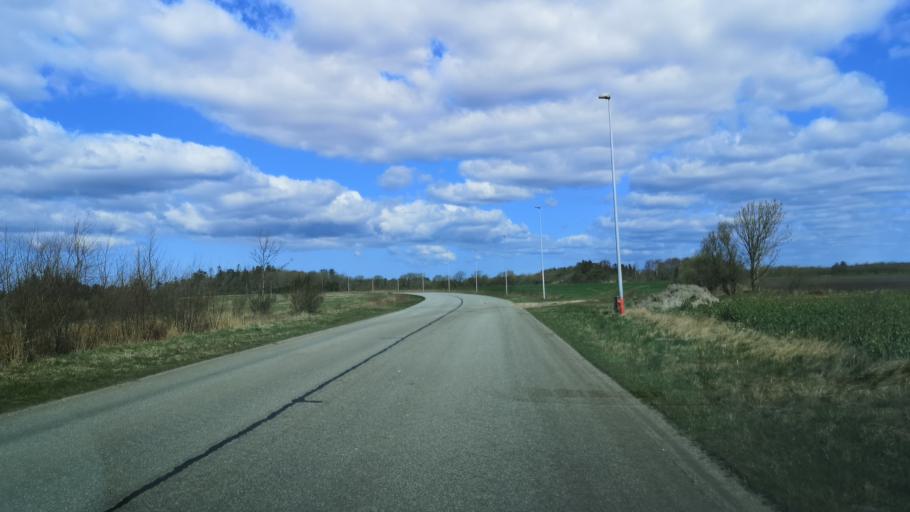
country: DK
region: Central Jutland
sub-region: Ringkobing-Skjern Kommune
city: Skjern
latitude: 55.9594
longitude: 8.5127
